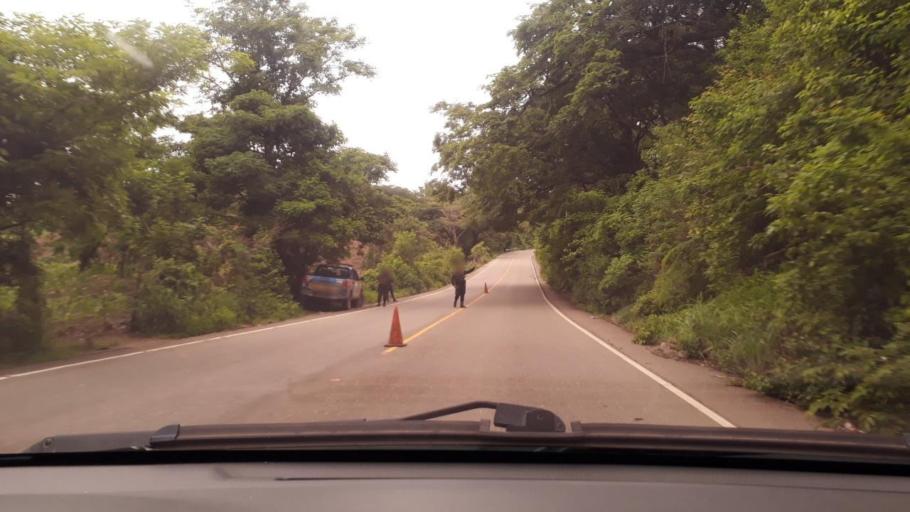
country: GT
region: Chiquimula
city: Concepcion Las Minas
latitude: 14.4584
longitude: -89.4645
